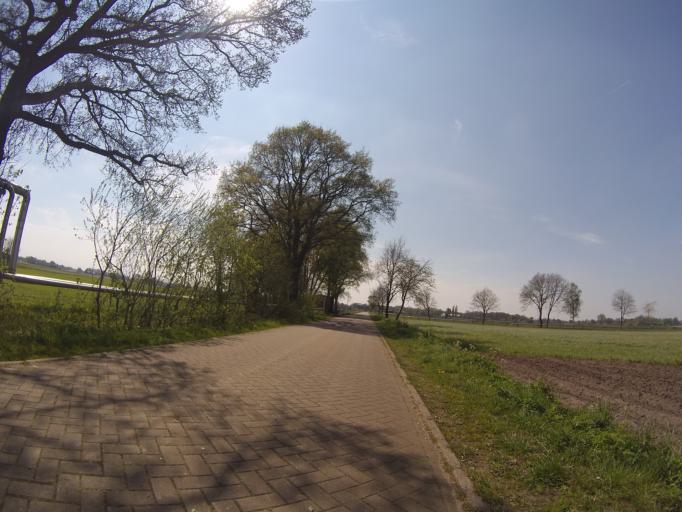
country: NL
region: Drenthe
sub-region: Gemeente Emmen
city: Schoonebeek
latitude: 52.6481
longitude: 6.8947
